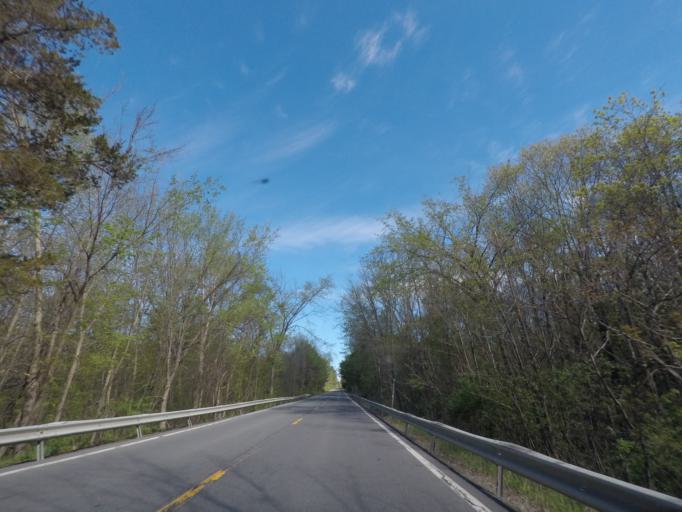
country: US
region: New York
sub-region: Albany County
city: Ravena
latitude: 42.4928
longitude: -73.9409
